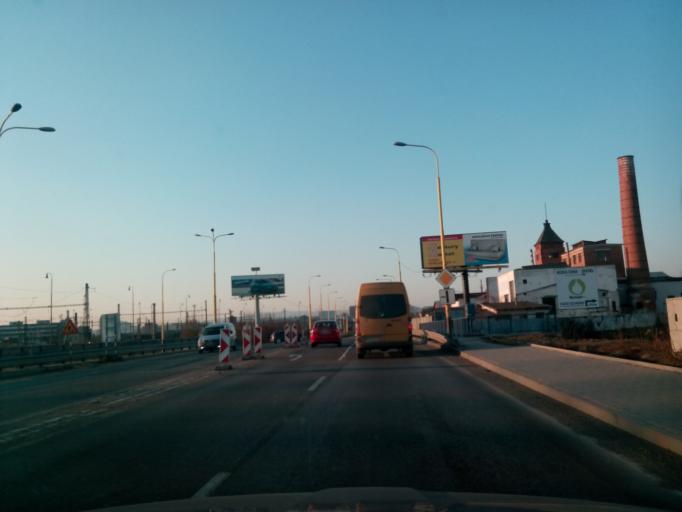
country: SK
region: Presovsky
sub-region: Okres Presov
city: Presov
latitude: 48.9763
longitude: 21.2519
